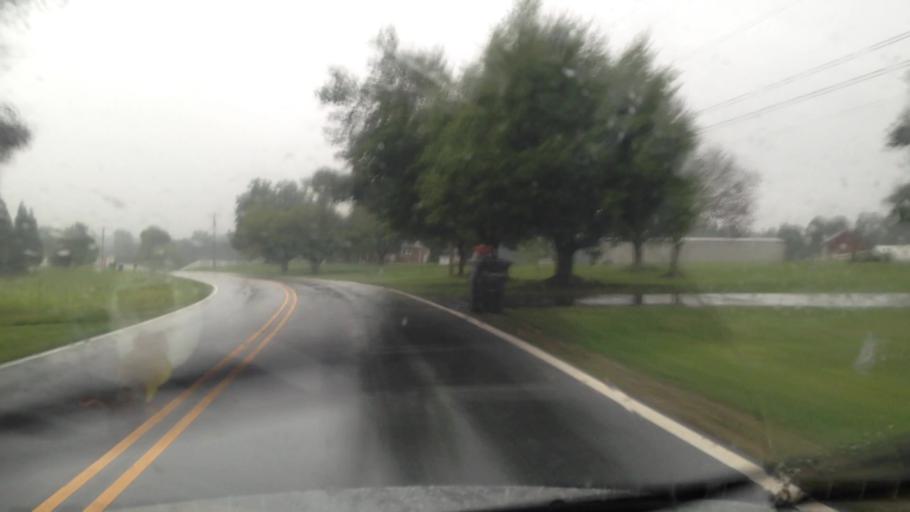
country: US
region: North Carolina
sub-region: Forsyth County
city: Kernersville
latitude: 36.1478
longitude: -80.0881
